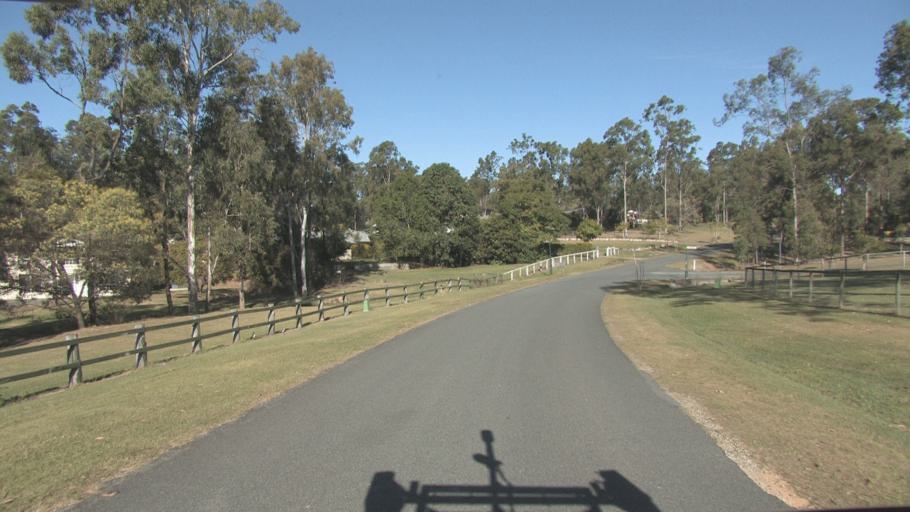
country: AU
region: Queensland
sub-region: Ipswich
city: Springfield Lakes
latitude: -27.7316
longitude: 152.9287
